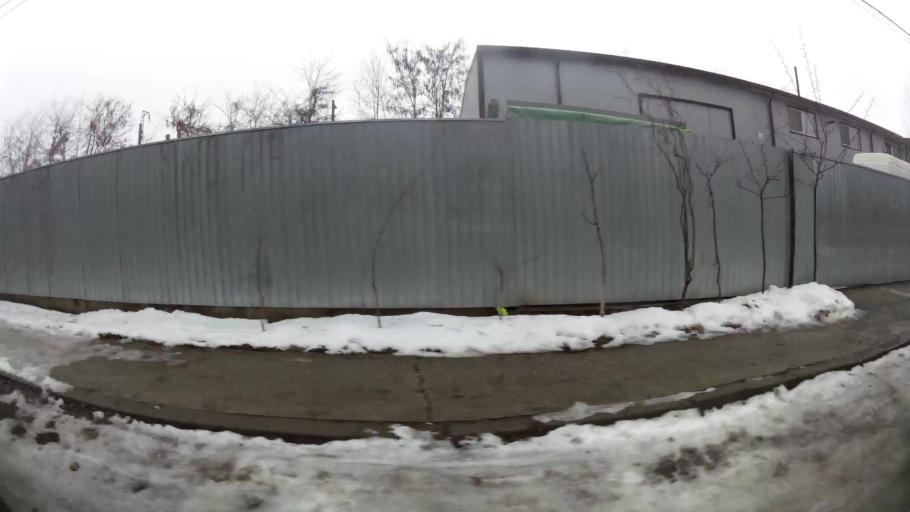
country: RO
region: Ilfov
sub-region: Comuna Chiajna
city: Chiajna
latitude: 44.4661
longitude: 25.9754
